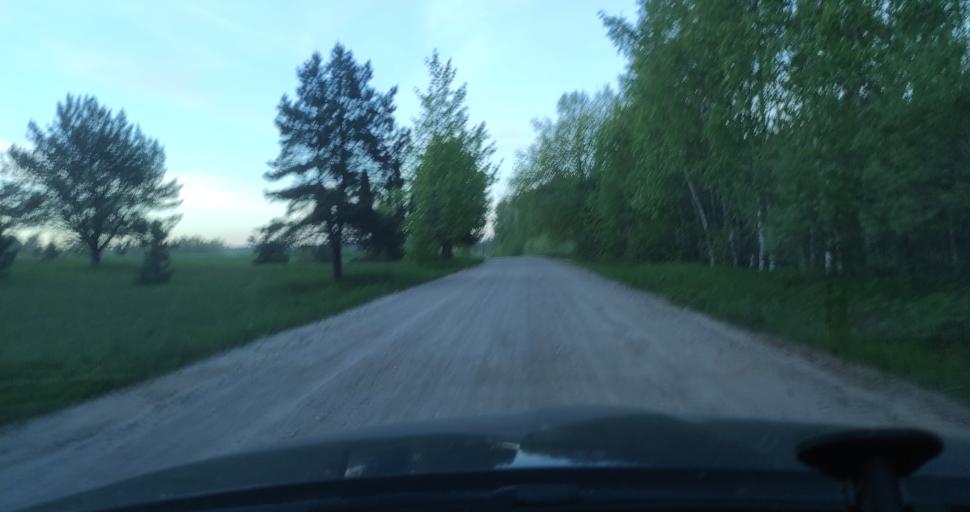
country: LV
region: Kuldigas Rajons
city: Kuldiga
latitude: 56.9511
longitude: 21.9163
